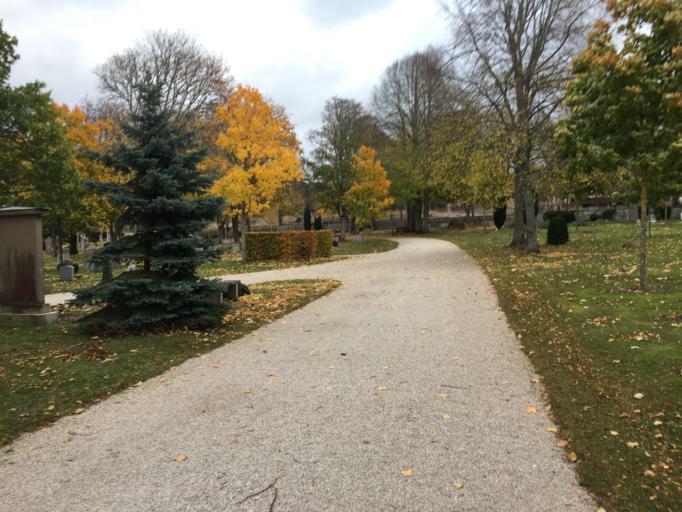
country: SE
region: Gotland
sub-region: Gotland
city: Visby
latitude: 57.6578
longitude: 18.3147
